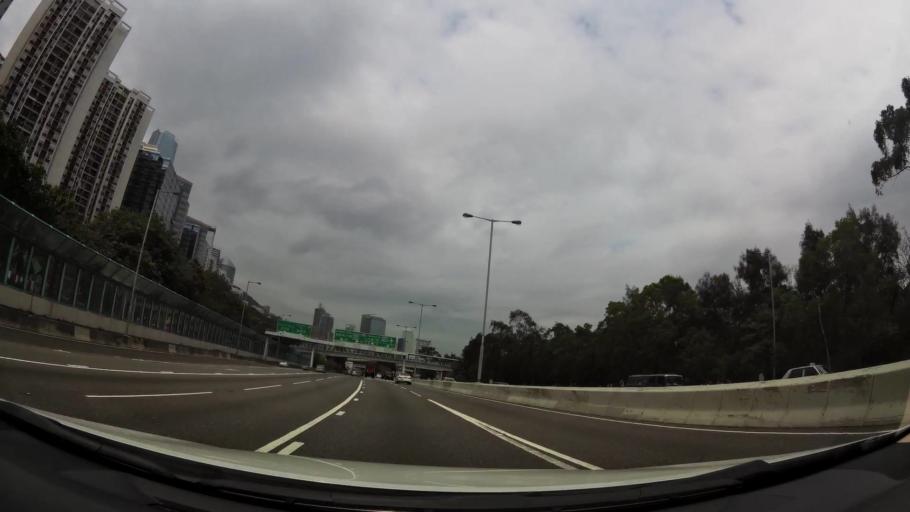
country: HK
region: Kowloon City
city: Kowloon
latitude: 22.2885
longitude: 114.2198
